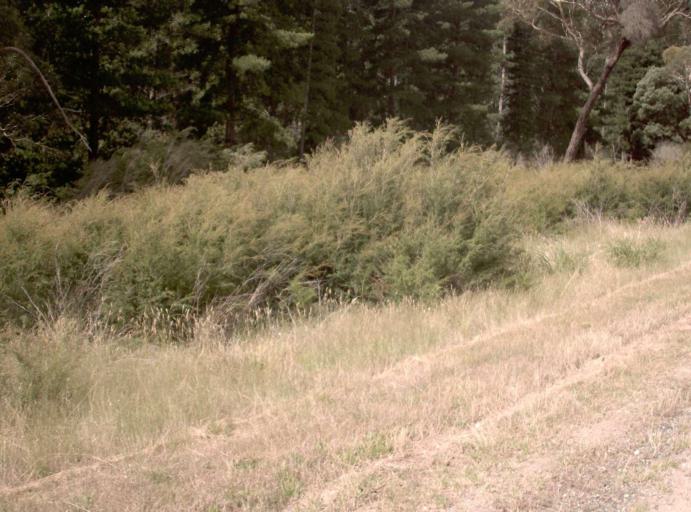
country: AU
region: Victoria
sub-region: Wellington
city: Sale
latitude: -38.1718
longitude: 146.9898
